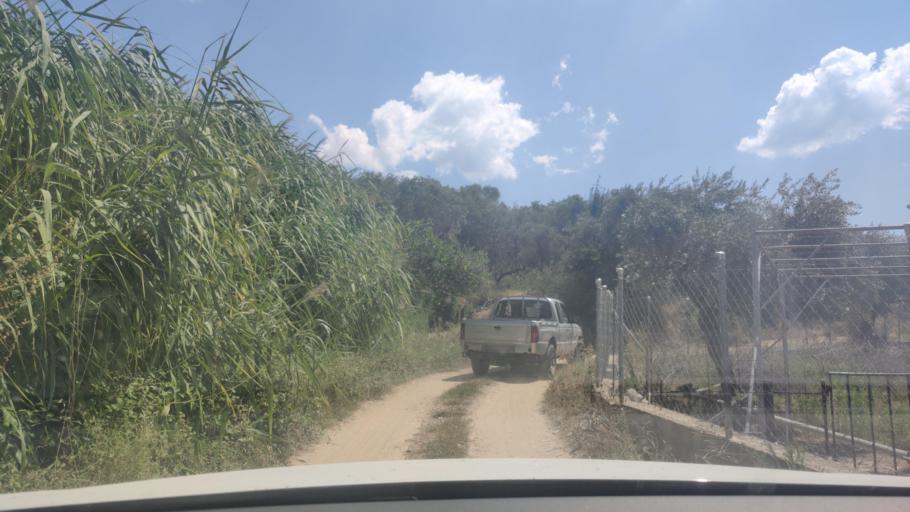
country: GR
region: East Macedonia and Thrace
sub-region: Nomos Kavalas
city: Limenaria
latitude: 40.6382
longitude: 24.5243
